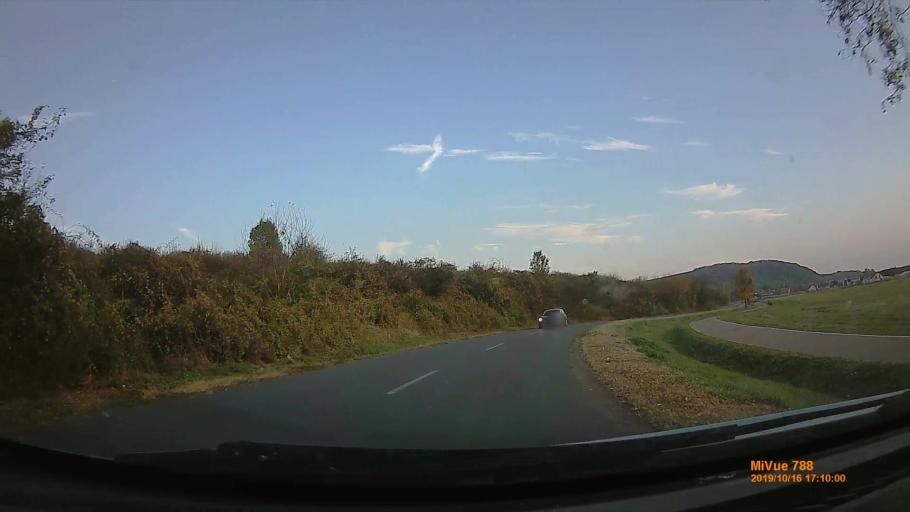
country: HU
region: Heves
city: Egerszalok
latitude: 47.8461
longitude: 20.3315
